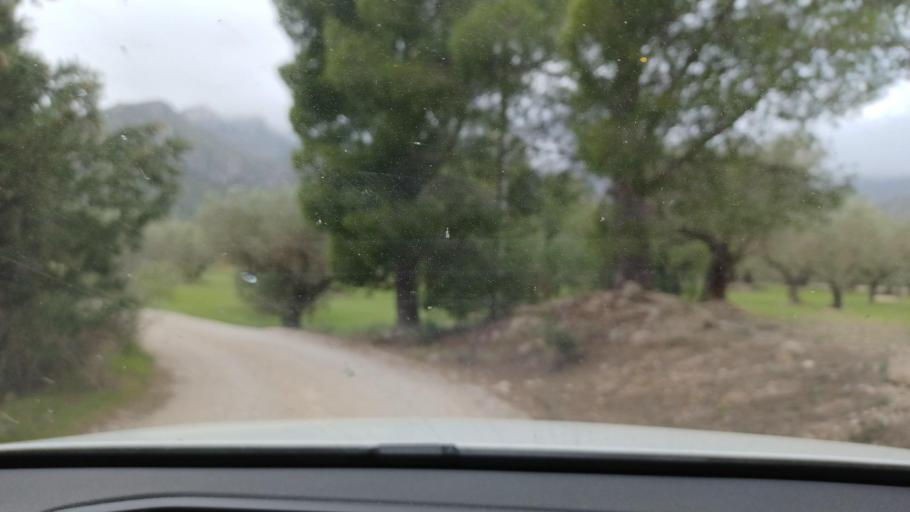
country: ES
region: Catalonia
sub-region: Provincia de Tarragona
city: Mas de Barberans
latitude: 40.8037
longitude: 0.4113
